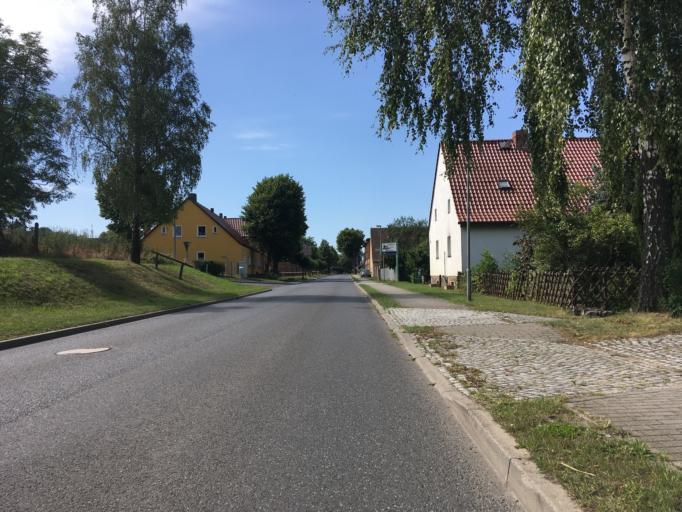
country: DE
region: Brandenburg
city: Zichow
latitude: 53.1904
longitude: 14.0385
